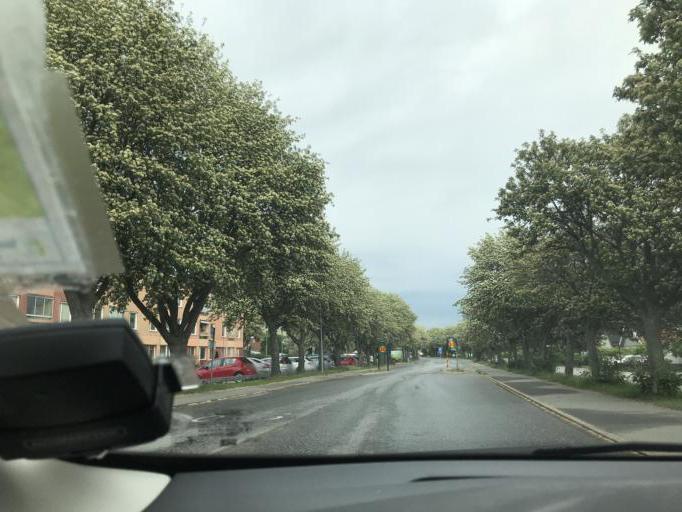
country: SE
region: Stockholm
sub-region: Botkyrka Kommun
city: Tumba
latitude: 59.2045
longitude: 17.8318
